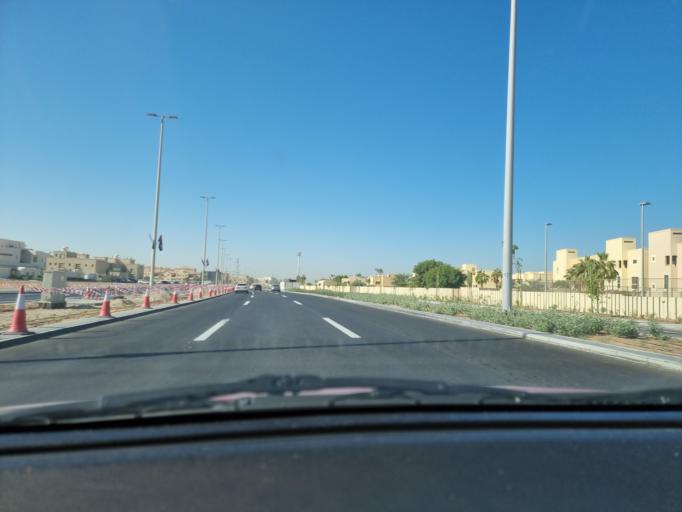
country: AE
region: Abu Dhabi
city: Abu Dhabi
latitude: 24.4380
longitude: 54.5904
